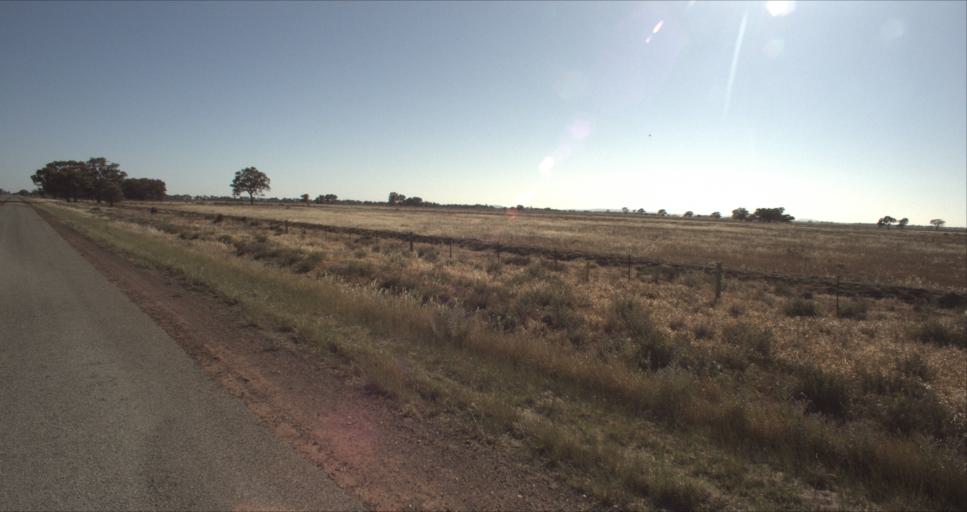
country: AU
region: New South Wales
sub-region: Leeton
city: Leeton
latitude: -34.5938
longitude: 146.2591
